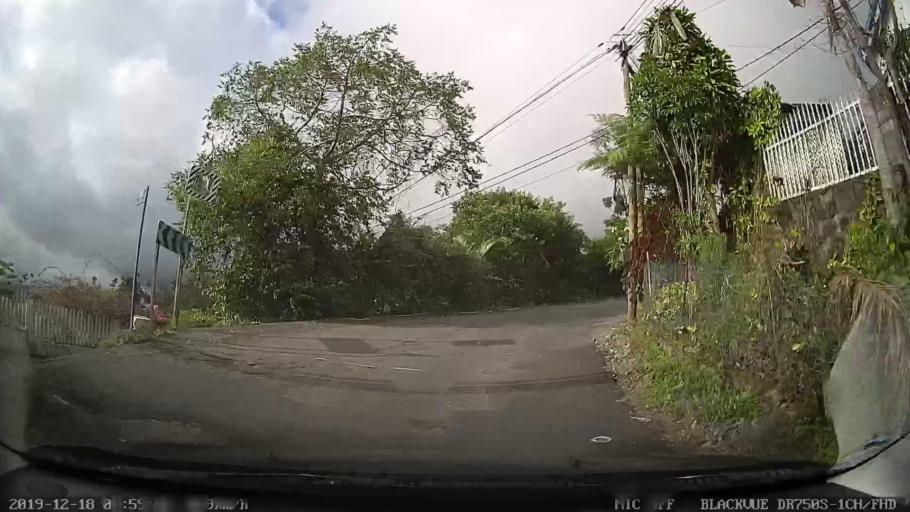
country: RE
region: Reunion
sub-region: Reunion
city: Le Tampon
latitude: -21.2553
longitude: 55.5164
